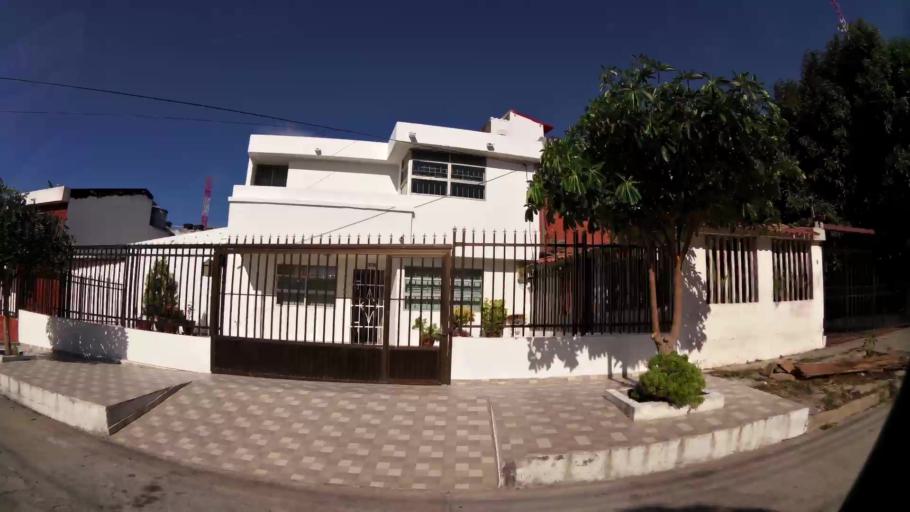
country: CO
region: Atlantico
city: Barranquilla
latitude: 10.9941
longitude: -74.8297
